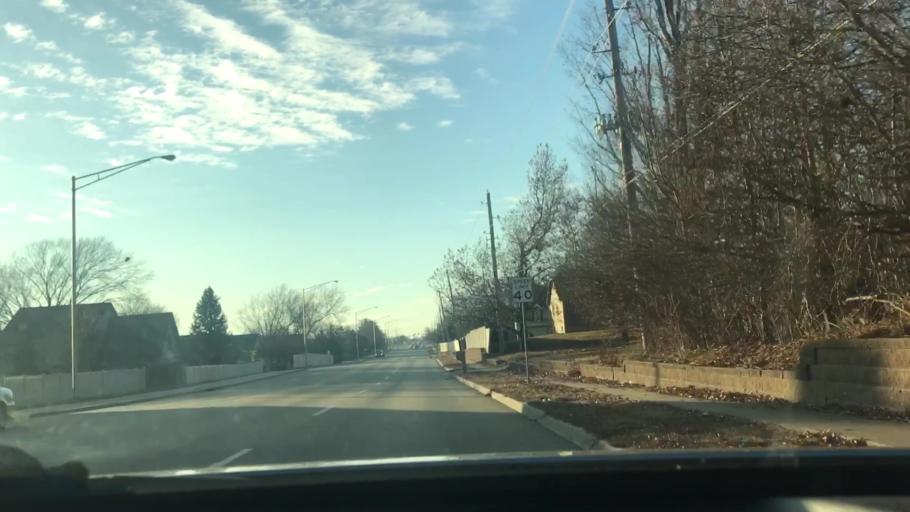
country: US
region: Missouri
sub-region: Jackson County
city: Lees Summit
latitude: 38.9315
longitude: -94.3524
